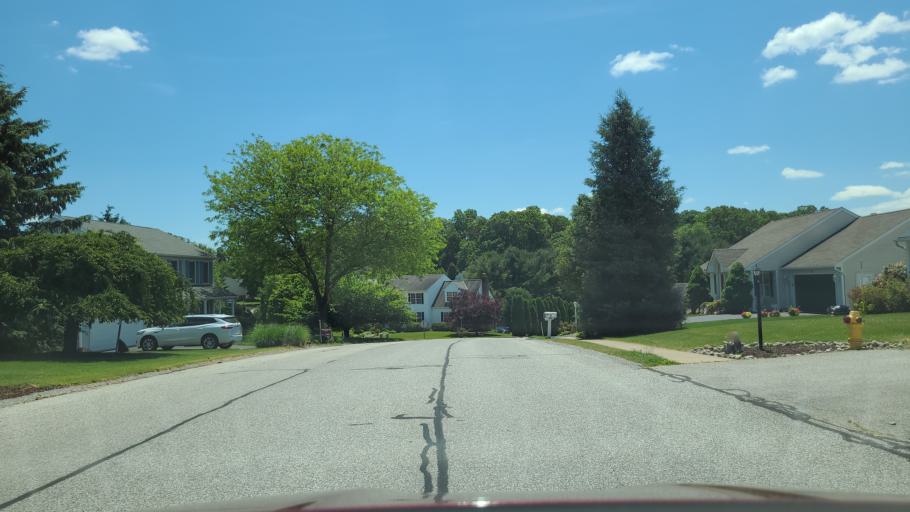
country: US
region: Pennsylvania
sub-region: York County
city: New Freedom
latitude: 39.7375
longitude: -76.6916
